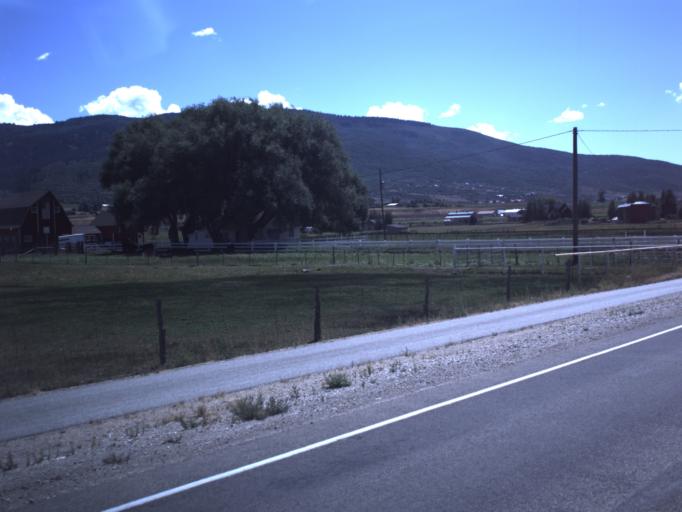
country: US
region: Utah
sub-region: Summit County
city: Oakley
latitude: 40.6998
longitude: -111.2811
